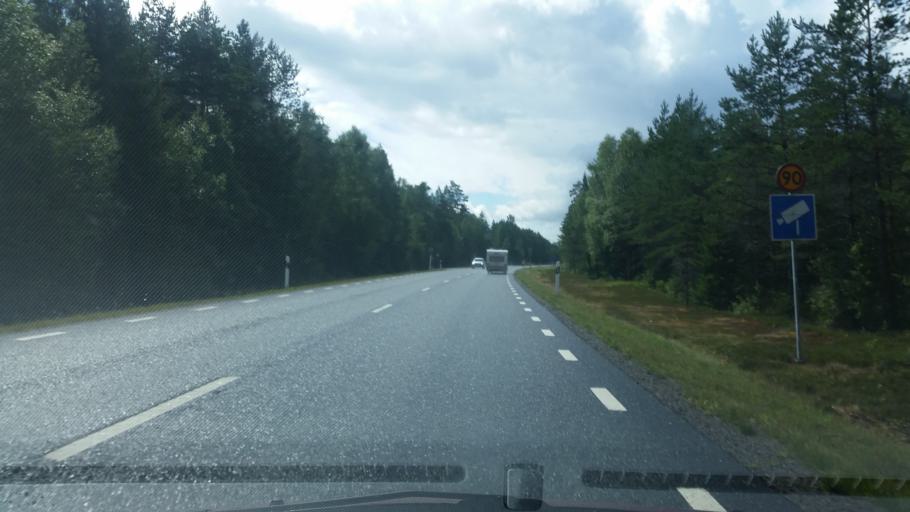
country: SE
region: Joenkoeping
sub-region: Gislaveds Kommun
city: Gislaved
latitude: 57.3892
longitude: 13.5883
